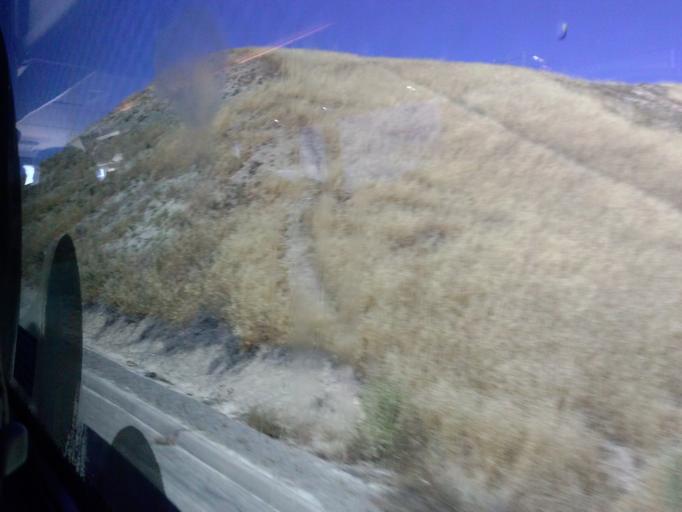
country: US
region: California
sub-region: Alameda County
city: Livermore
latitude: 37.6039
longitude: -121.6866
